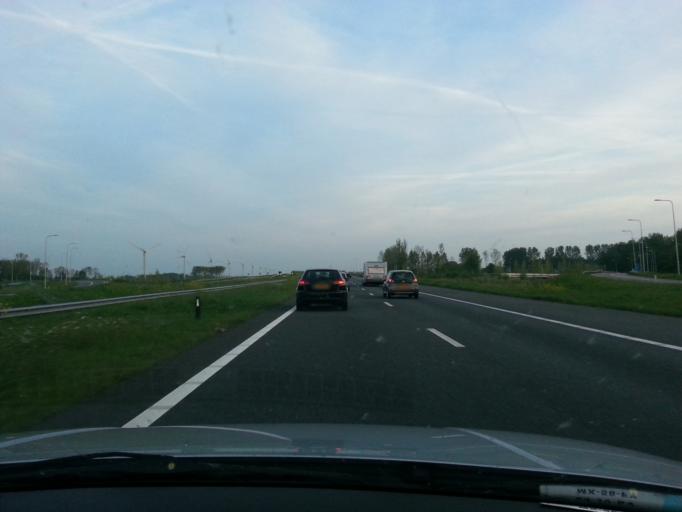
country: NL
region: Flevoland
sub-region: Gemeente Lelystad
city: Lelystad
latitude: 52.5553
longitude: 5.5304
